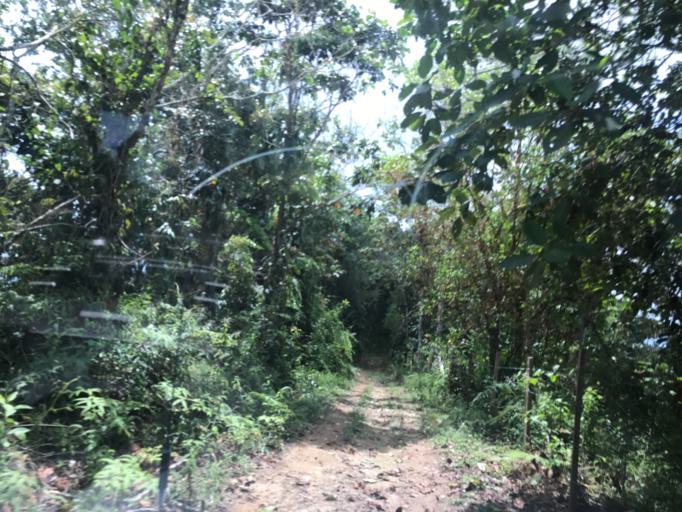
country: CO
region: Valle del Cauca
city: Obando
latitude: 4.5835
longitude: -75.8905
